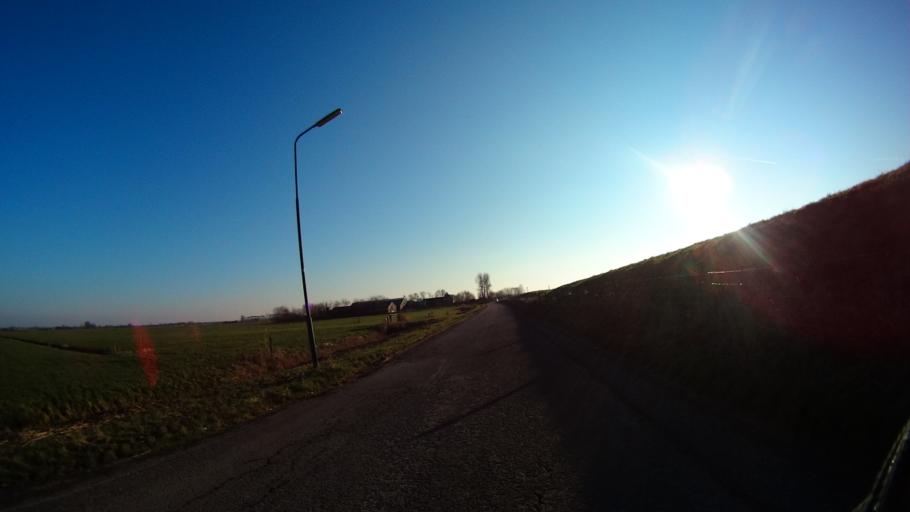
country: NL
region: Utrecht
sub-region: Gemeente Baarn
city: Baarn
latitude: 52.2124
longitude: 5.3114
